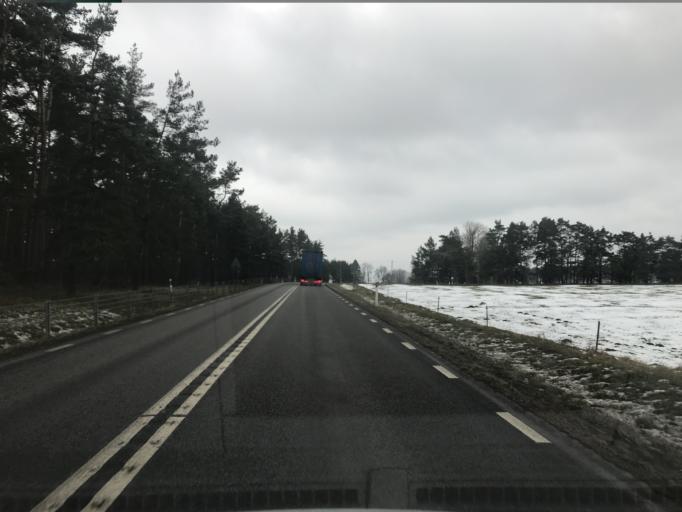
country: SE
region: Skane
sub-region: Kristianstads Kommun
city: Degeberga
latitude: 55.8774
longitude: 14.0877
